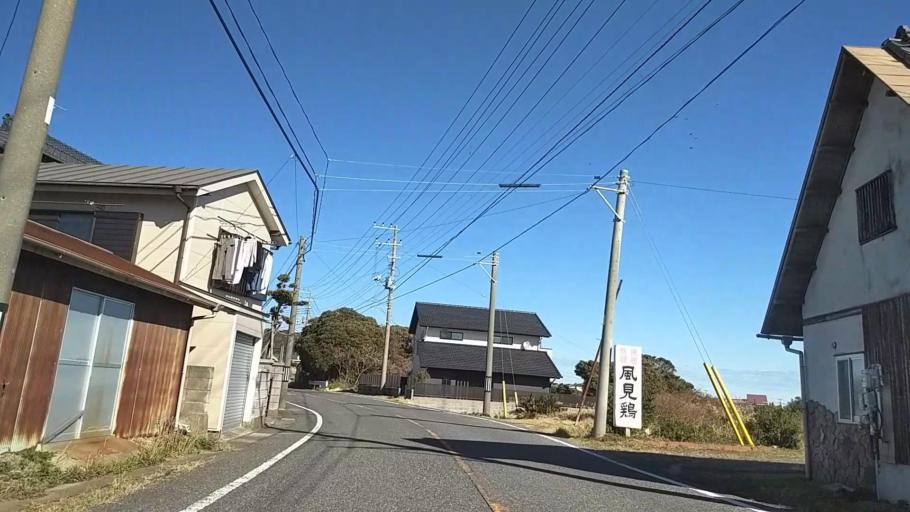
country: JP
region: Chiba
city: Tateyama
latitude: 34.9398
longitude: 139.9563
